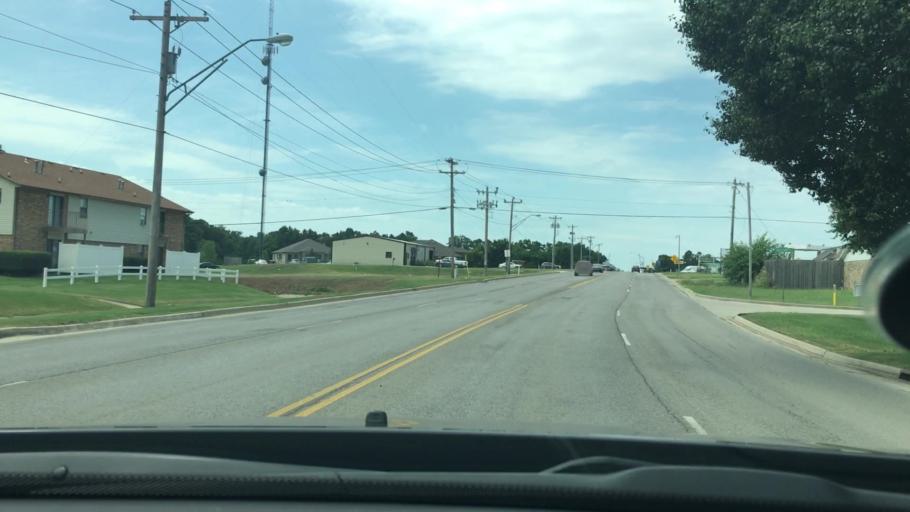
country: US
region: Oklahoma
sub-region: Carter County
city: Ardmore
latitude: 34.1811
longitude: -97.1606
